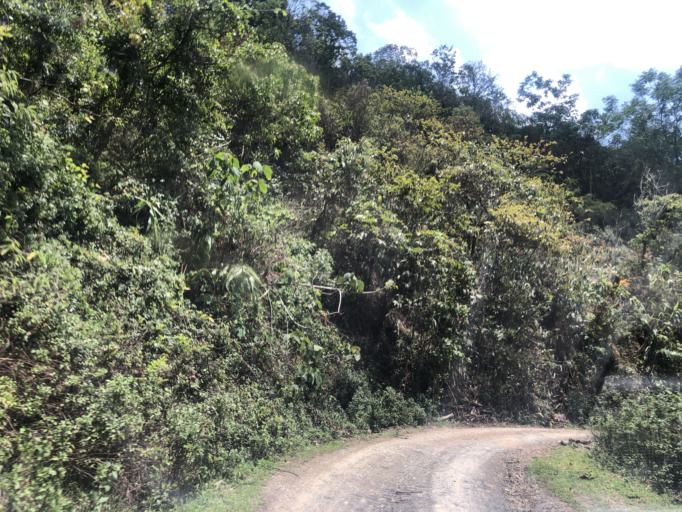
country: LA
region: Phongsali
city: Phongsali
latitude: 21.4443
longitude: 102.1638
